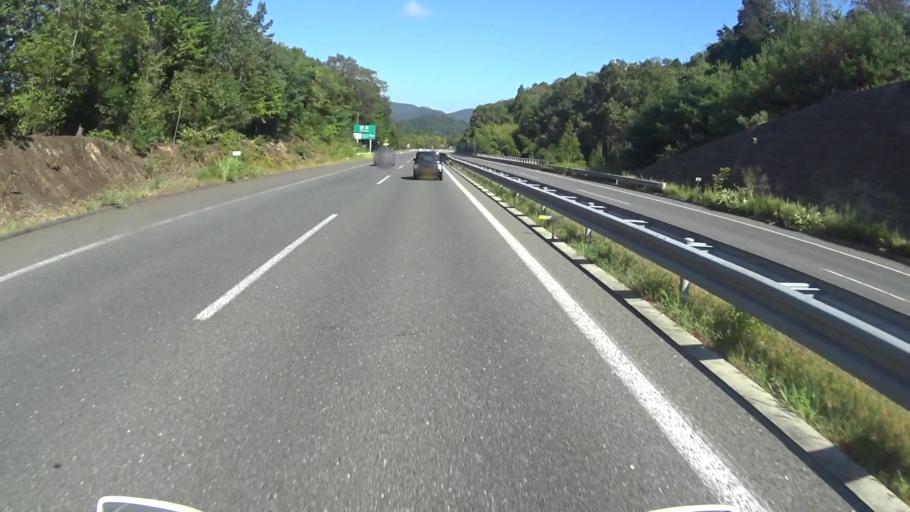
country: JP
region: Kyoto
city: Kameoka
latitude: 35.1105
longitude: 135.4814
